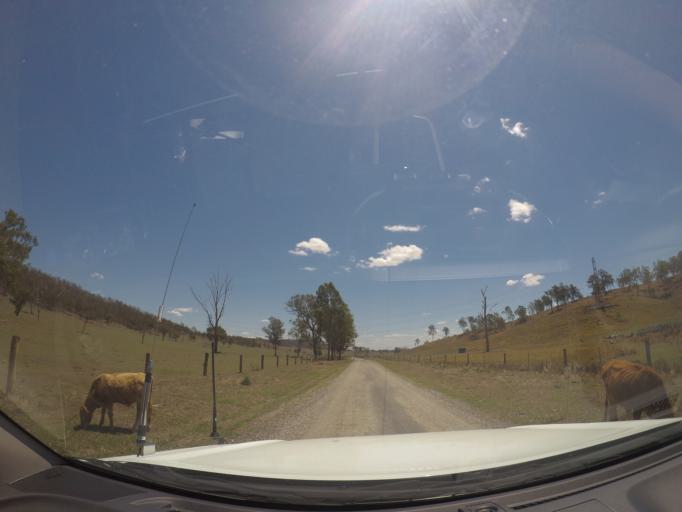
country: AU
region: Queensland
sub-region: Ipswich
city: Redbank Plains
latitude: -27.7525
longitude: 152.8337
